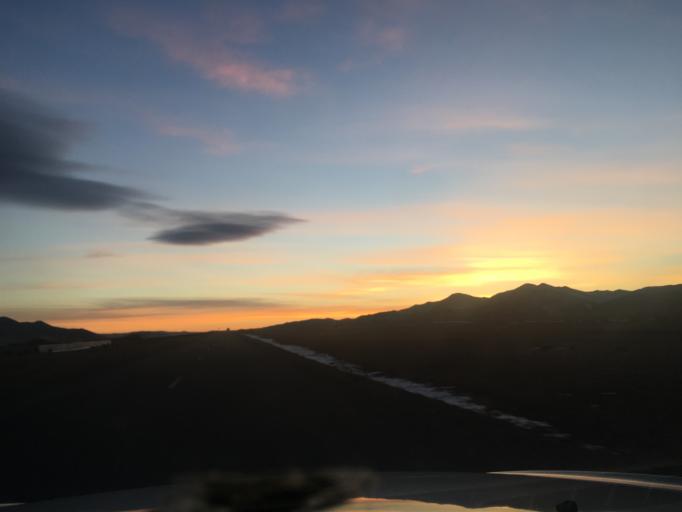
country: MN
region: Central Aimak
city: Mandal
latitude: 48.1028
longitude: 106.6233
